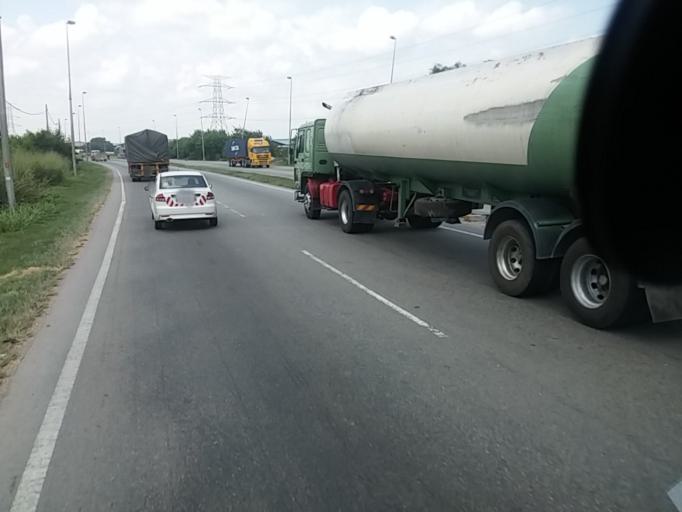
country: MY
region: Selangor
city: Klang
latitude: 2.9778
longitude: 101.3943
